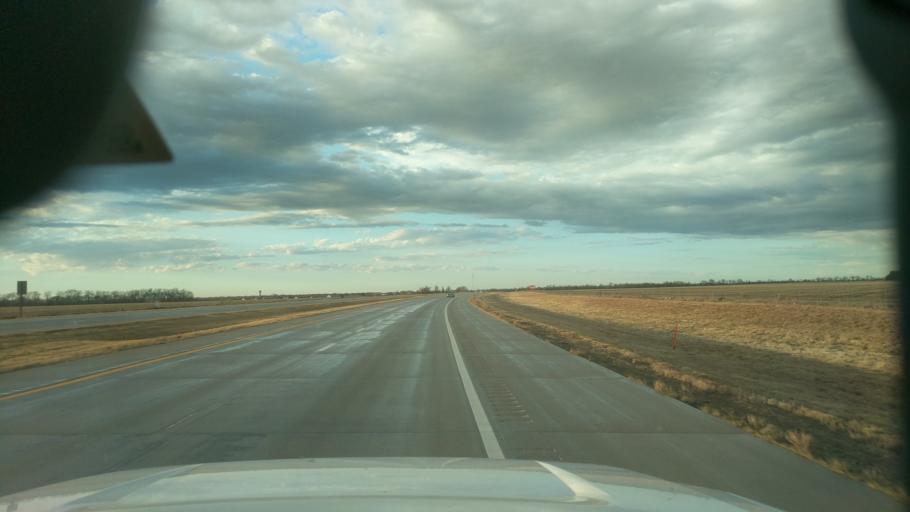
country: US
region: Kansas
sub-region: Harvey County
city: Hesston
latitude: 38.1188
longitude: -97.3917
